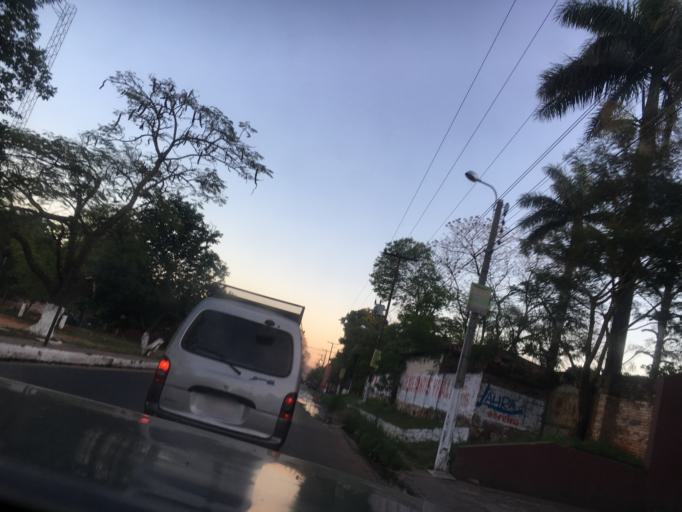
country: PY
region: Central
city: Lambare
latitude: -25.3490
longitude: -57.6008
